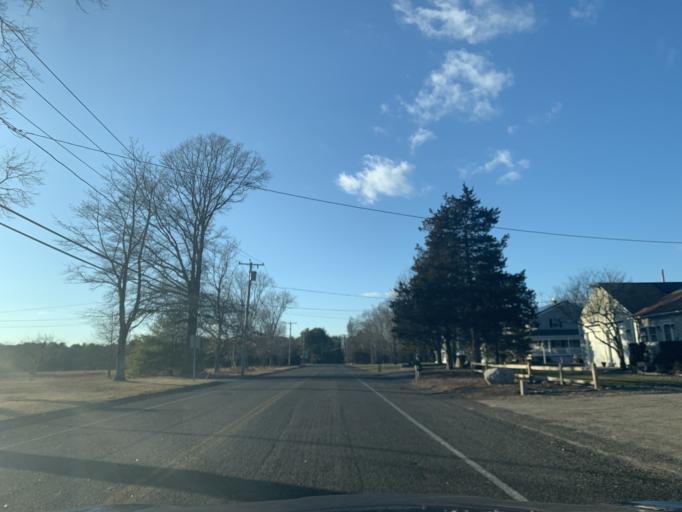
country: US
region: Massachusetts
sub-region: Bristol County
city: Norton
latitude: 41.9033
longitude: -71.2154
